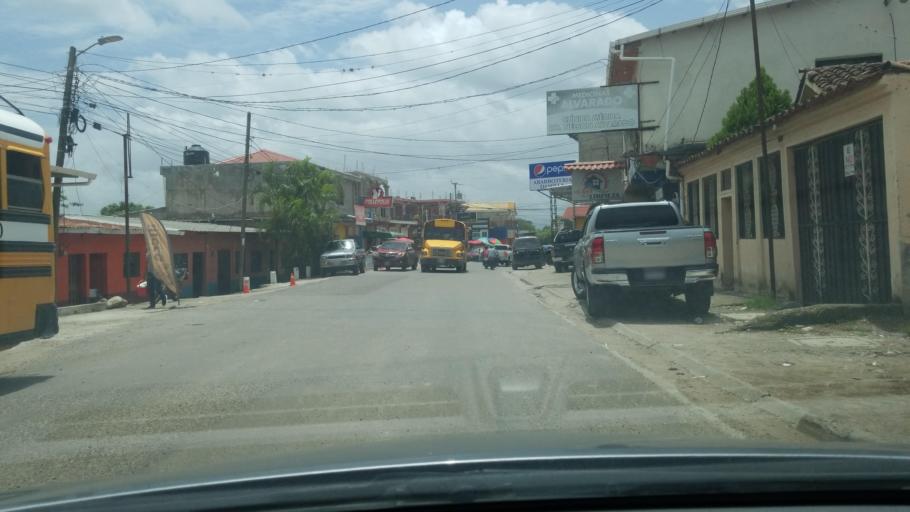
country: HN
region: Copan
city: Cucuyagua
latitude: 14.6500
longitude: -88.8763
